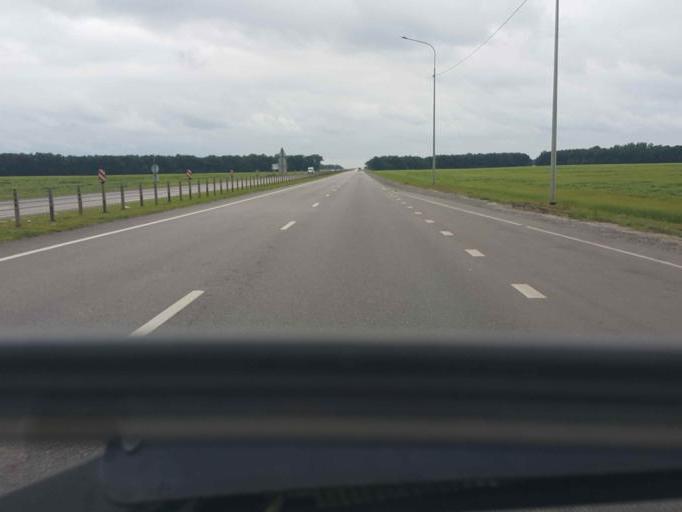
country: RU
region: Tambov
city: Zavoronezhskoye
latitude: 52.8926
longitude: 40.6918
